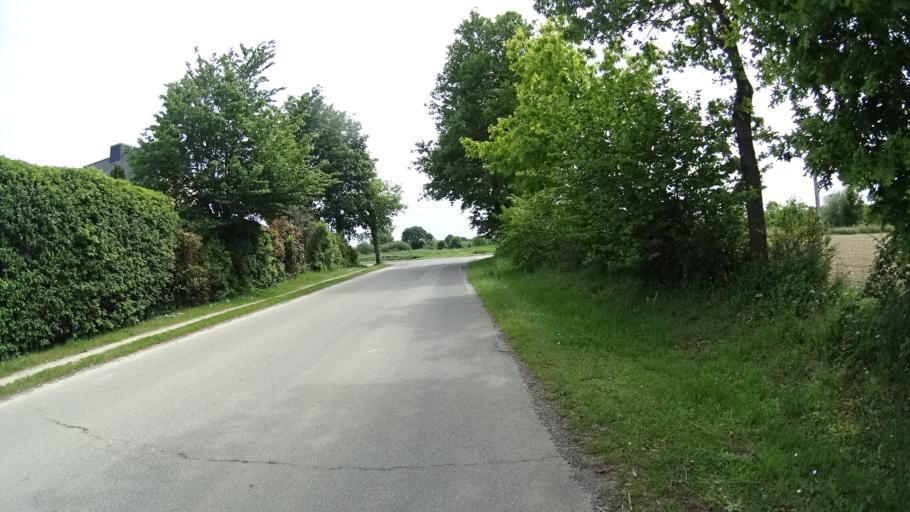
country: FR
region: Brittany
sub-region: Departement d'Ille-et-Vilaine
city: La Meziere
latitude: 48.2201
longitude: -1.7627
